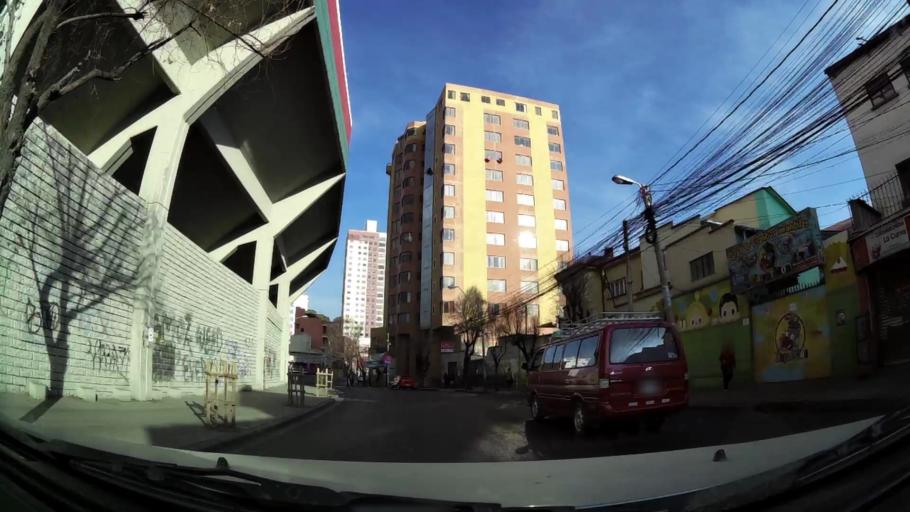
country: BO
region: La Paz
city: La Paz
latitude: -16.4985
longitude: -68.1224
